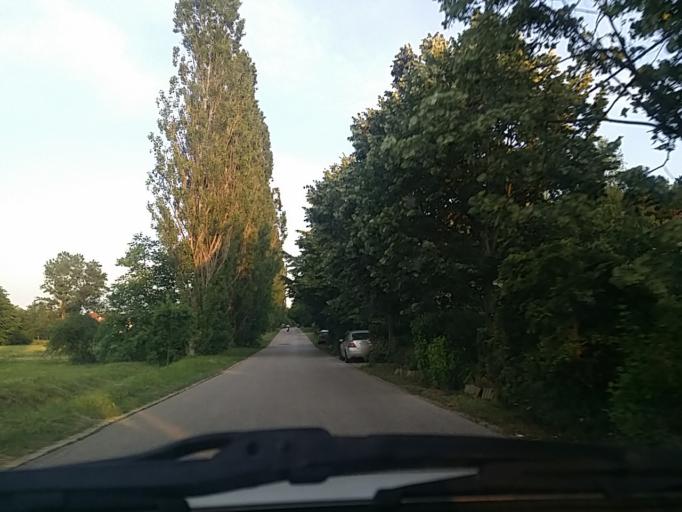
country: HU
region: Pest
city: Solymar
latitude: 47.5640
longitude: 18.9499
